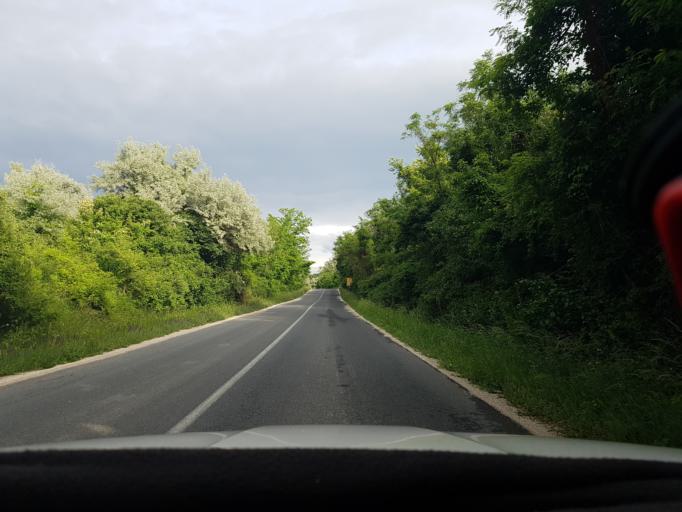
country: HU
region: Komarom-Esztergom
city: Nyergesujfalu
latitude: 47.7277
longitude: 18.5342
